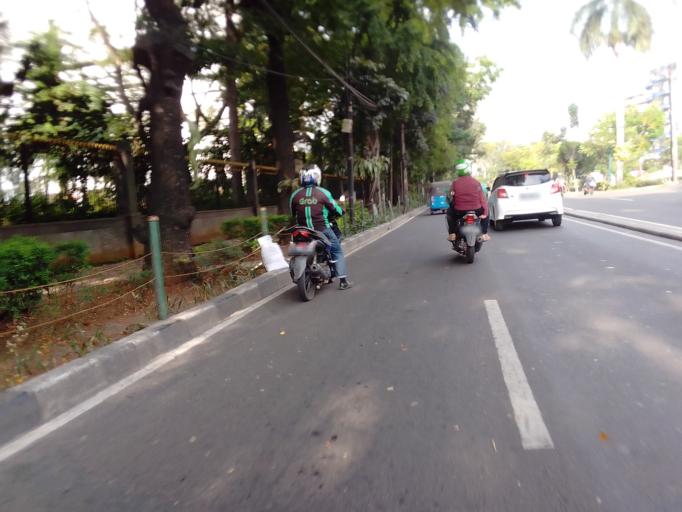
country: ID
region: Jakarta Raya
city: Jakarta
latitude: -6.1828
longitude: 106.8197
